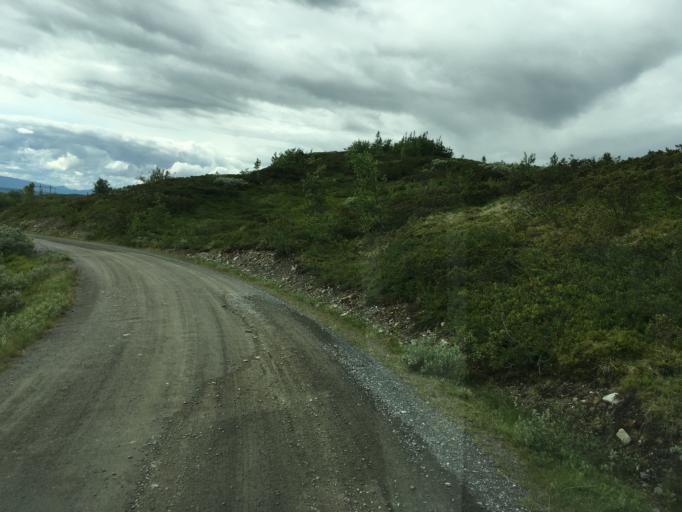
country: NO
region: Oppland
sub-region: Ringebu
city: Ringebu
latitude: 61.3632
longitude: 10.0355
